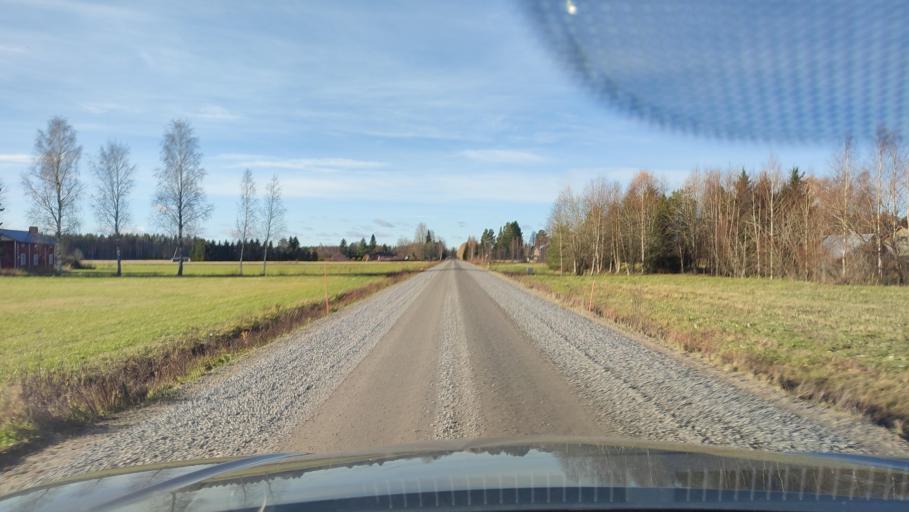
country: FI
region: Southern Ostrobothnia
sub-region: Suupohja
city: Teuva
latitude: 62.4568
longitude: 21.6382
